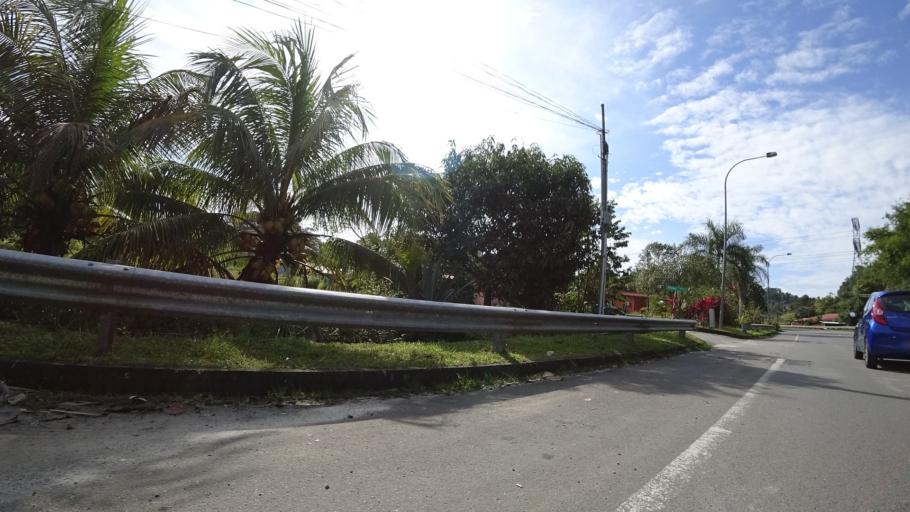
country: BN
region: Brunei and Muara
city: Bandar Seri Begawan
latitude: 4.8745
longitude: 114.8053
